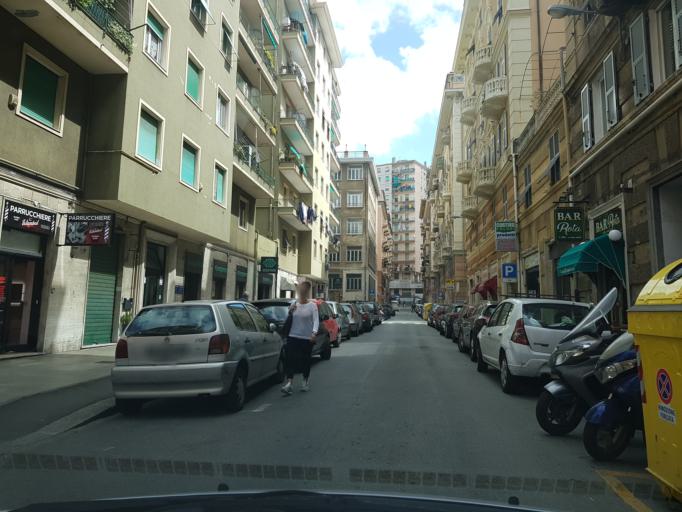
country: IT
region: Liguria
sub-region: Provincia di Genova
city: San Teodoro
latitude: 44.4145
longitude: 8.8886
